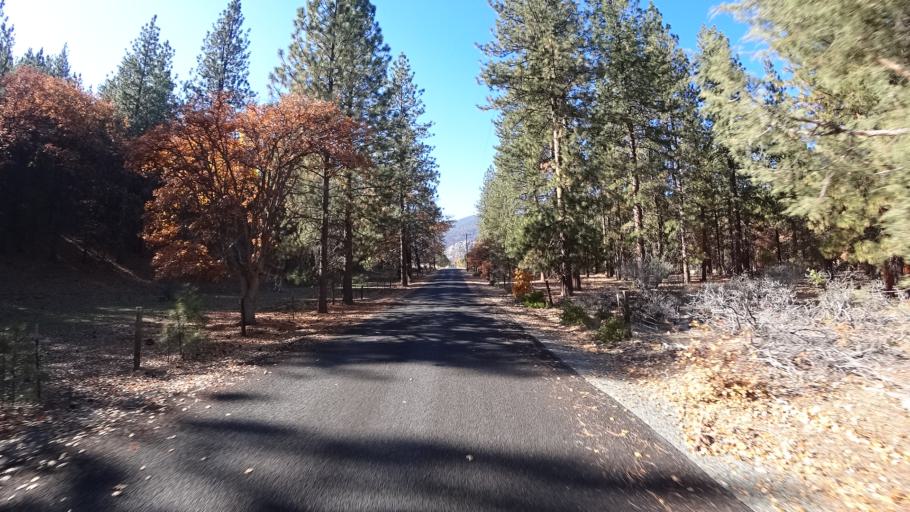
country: US
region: California
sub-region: Siskiyou County
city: Weed
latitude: 41.5035
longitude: -122.5813
